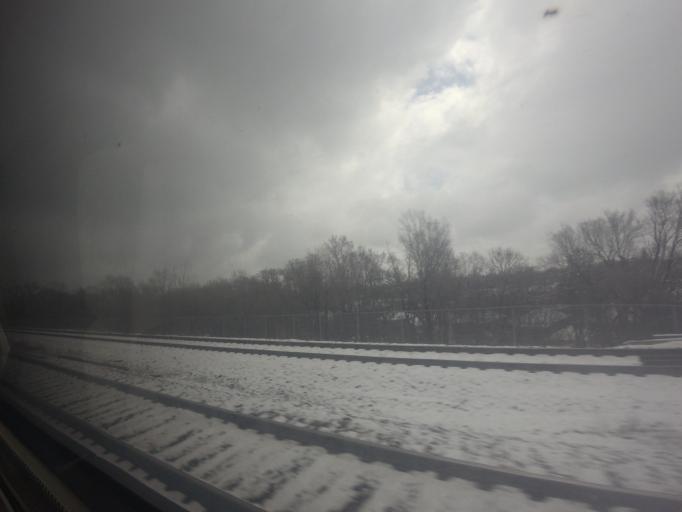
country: CA
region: Ontario
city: Scarborough
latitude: 43.6935
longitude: -79.2732
